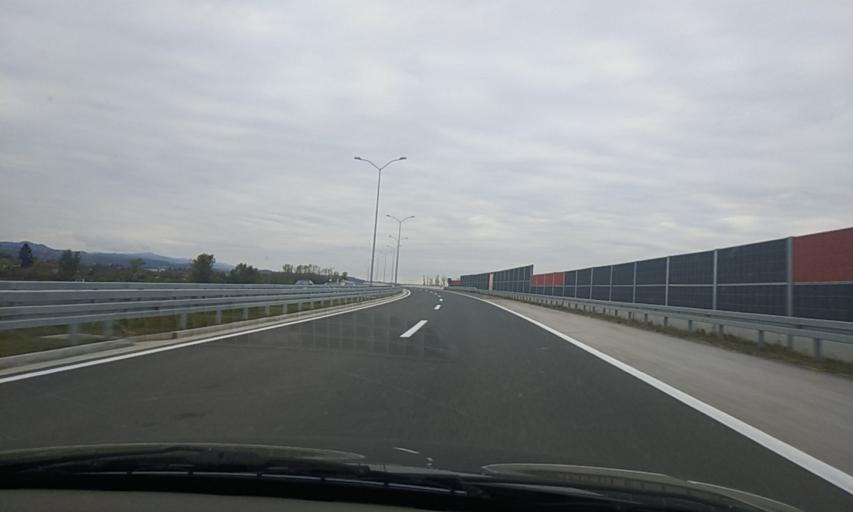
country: BA
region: Republika Srpska
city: Maglajani
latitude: 44.9132
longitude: 17.3412
